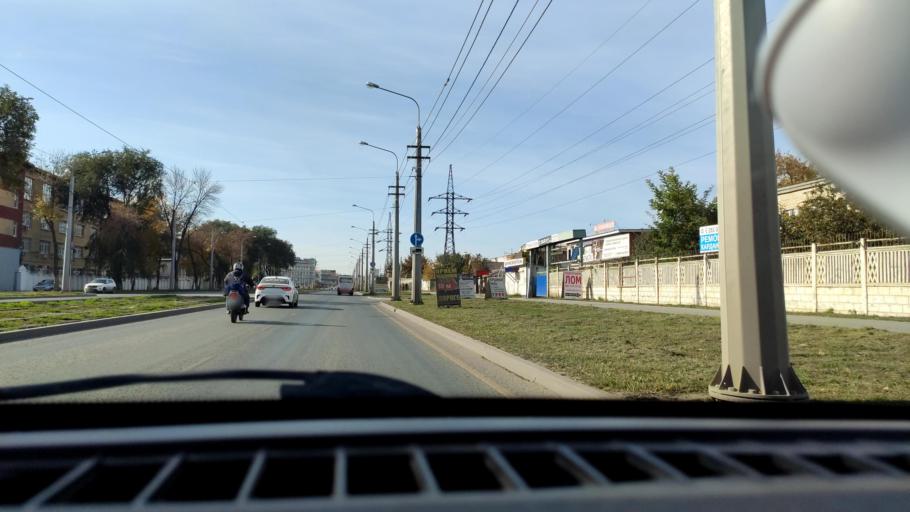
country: RU
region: Samara
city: Samara
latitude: 53.1979
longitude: 50.2535
